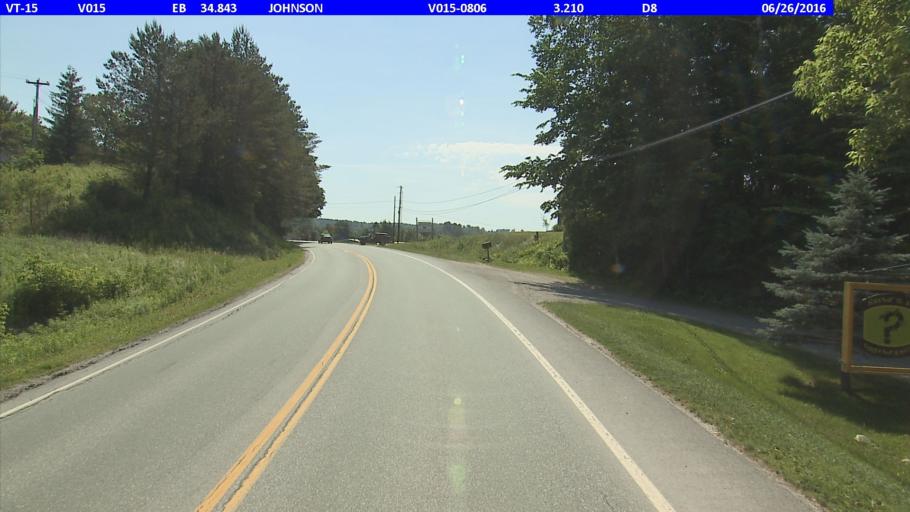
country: US
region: Vermont
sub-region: Lamoille County
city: Johnson
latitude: 44.6363
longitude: -72.6966
